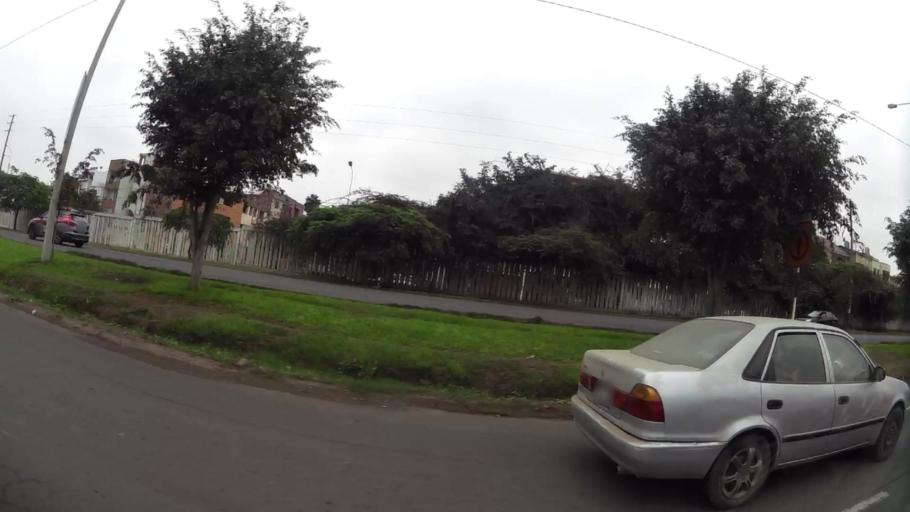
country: PE
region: Lima
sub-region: Lima
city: La Molina
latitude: -12.0617
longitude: -76.9383
